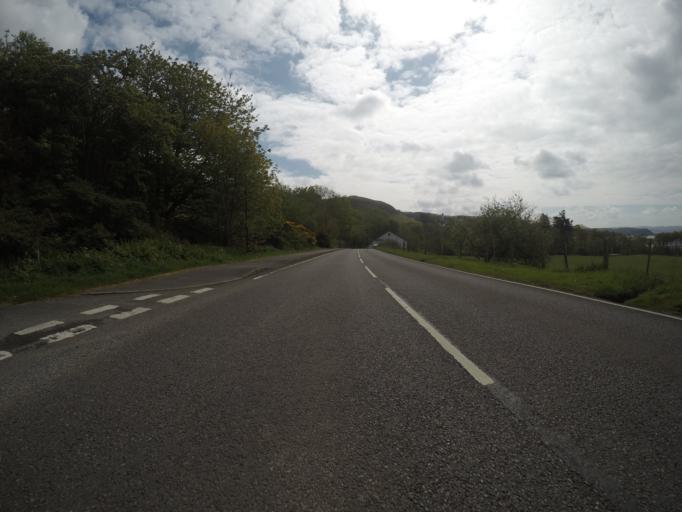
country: GB
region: Scotland
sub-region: Highland
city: Portree
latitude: 57.5909
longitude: -6.3554
